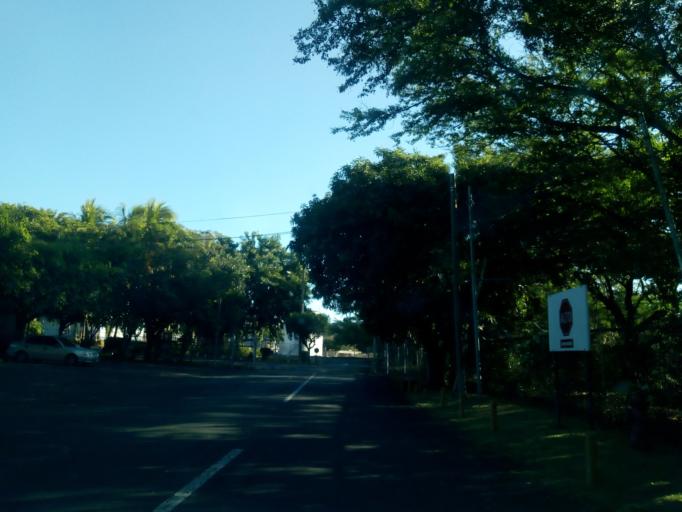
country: NI
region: Managua
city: Ciudad Sandino
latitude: 12.1485
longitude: -86.3196
